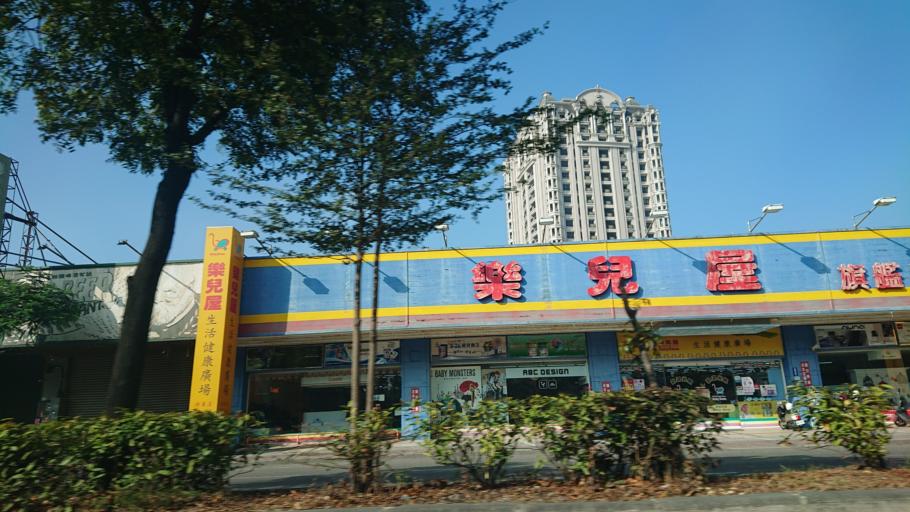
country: TW
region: Taiwan
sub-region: Tainan
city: Tainan
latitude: 23.0057
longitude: 120.1866
